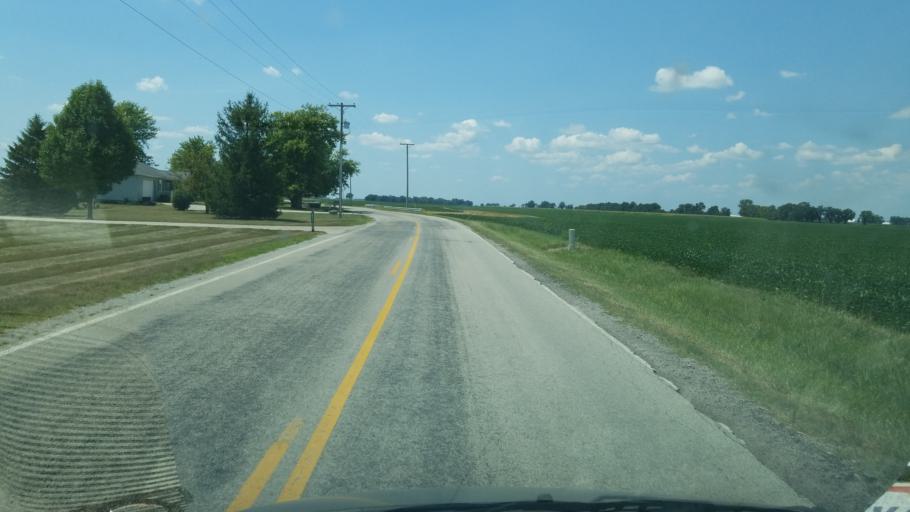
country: US
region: Ohio
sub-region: Madison County
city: Plain City
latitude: 40.0469
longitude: -83.3063
